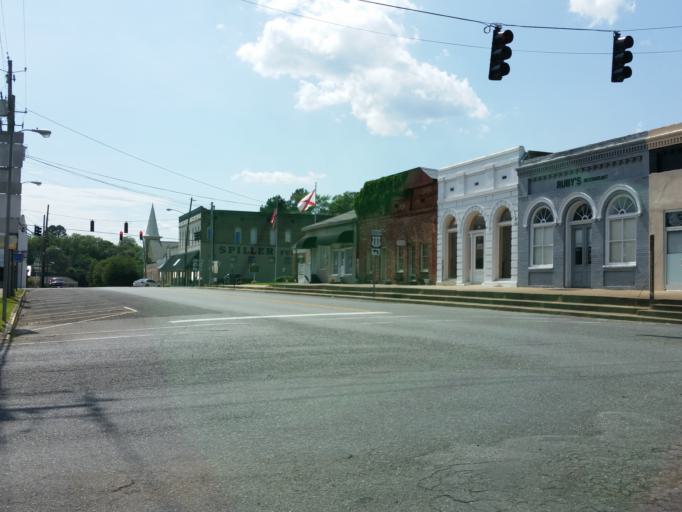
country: US
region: Alabama
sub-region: Greene County
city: Eutaw
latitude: 32.8409
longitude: -87.8869
